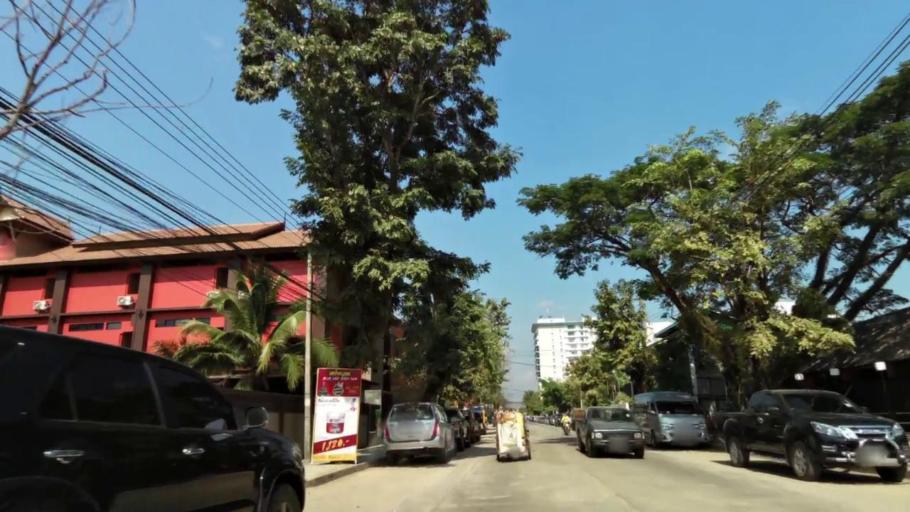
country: TH
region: Chiang Rai
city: Chiang Rai
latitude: 19.8976
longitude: 99.8278
